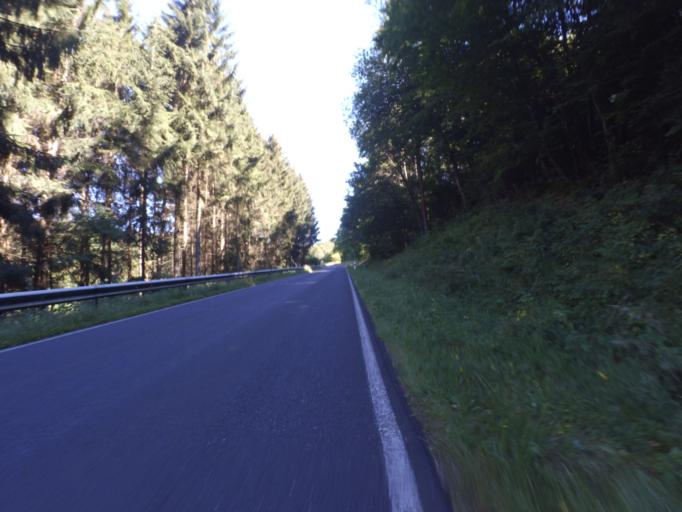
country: DE
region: Rheinland-Pfalz
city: Nohn
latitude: 50.3078
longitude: 6.7856
